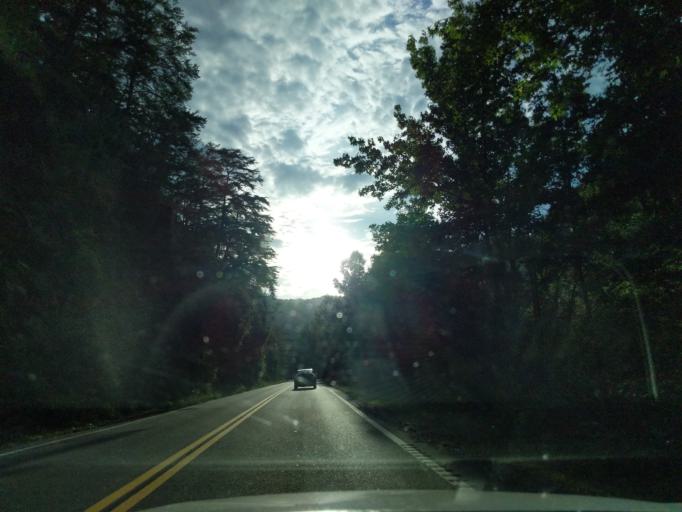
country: US
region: Tennessee
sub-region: Polk County
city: Benton
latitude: 35.0832
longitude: -84.5215
